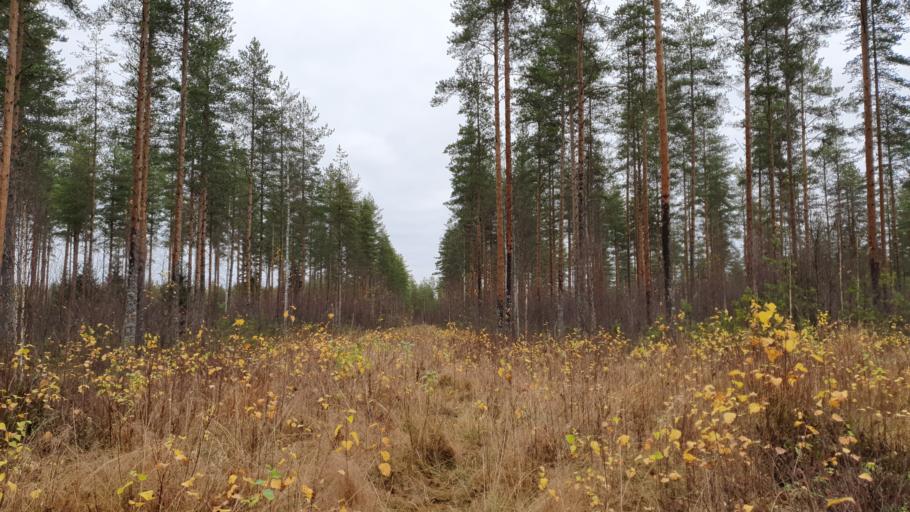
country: FI
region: Kainuu
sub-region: Kehys-Kainuu
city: Kuhmo
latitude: 64.1412
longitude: 29.4182
